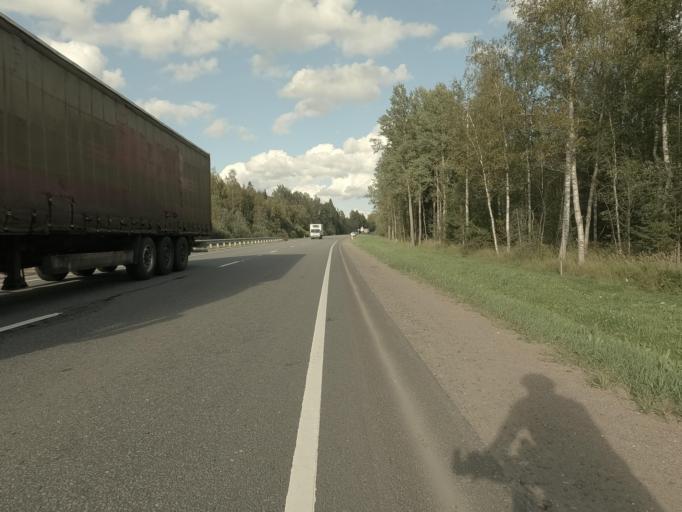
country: RU
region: Leningrad
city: Nikol'skoye
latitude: 59.6658
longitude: 30.8829
